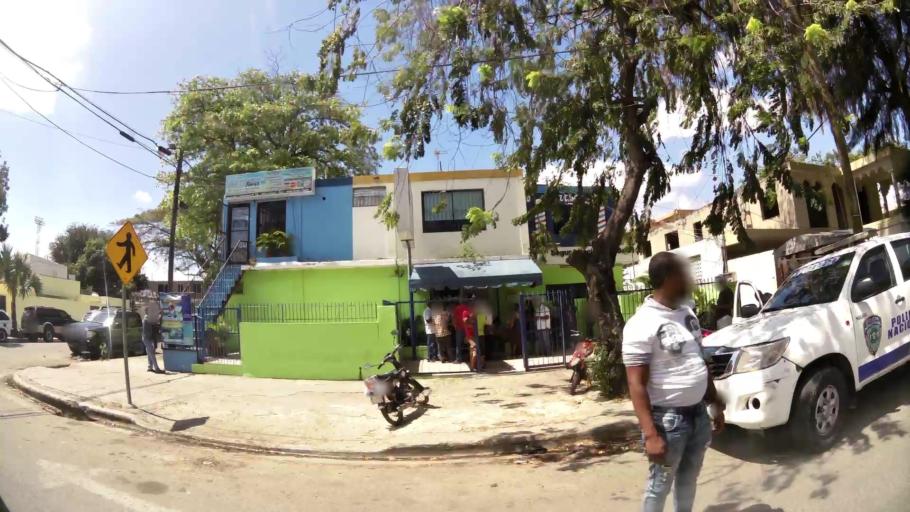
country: DO
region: San Cristobal
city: San Cristobal
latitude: 18.4149
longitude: -70.1068
